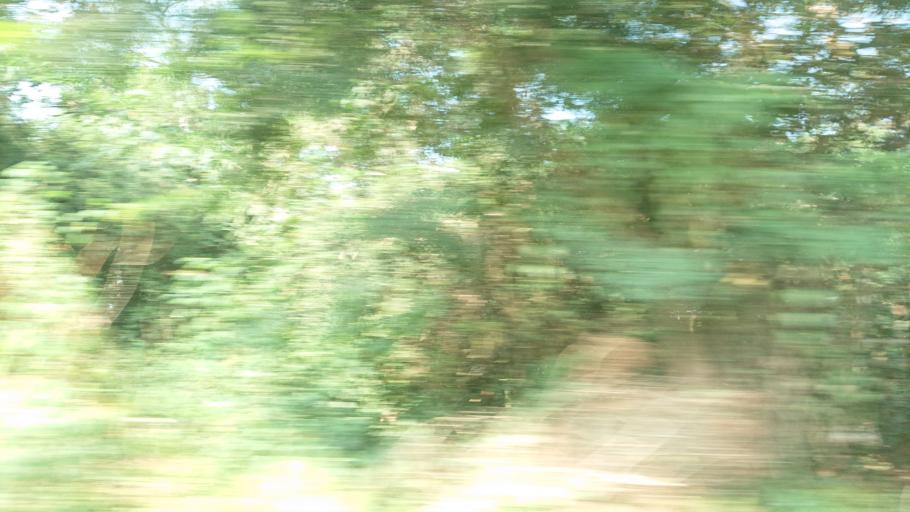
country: TW
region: Taiwan
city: Lugu
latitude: 23.7151
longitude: 120.6682
